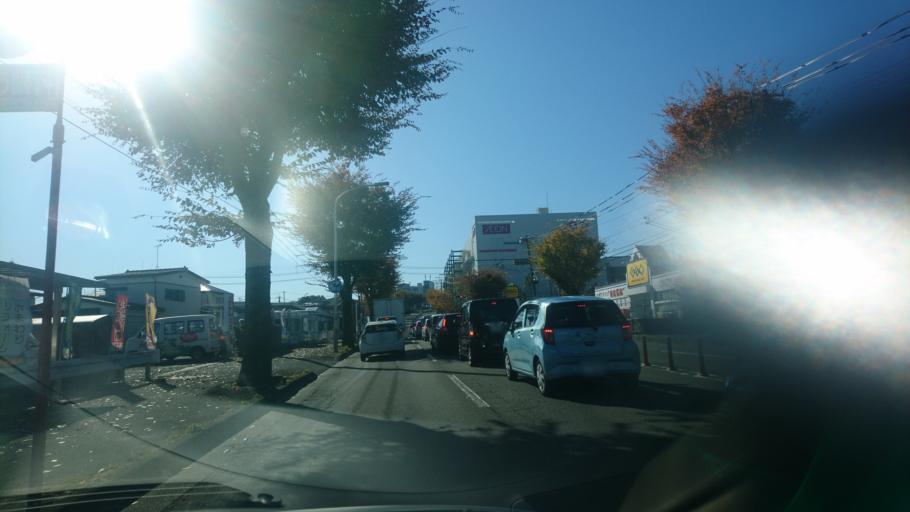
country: JP
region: Miyagi
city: Sendai-shi
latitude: 38.3004
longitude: 140.8298
